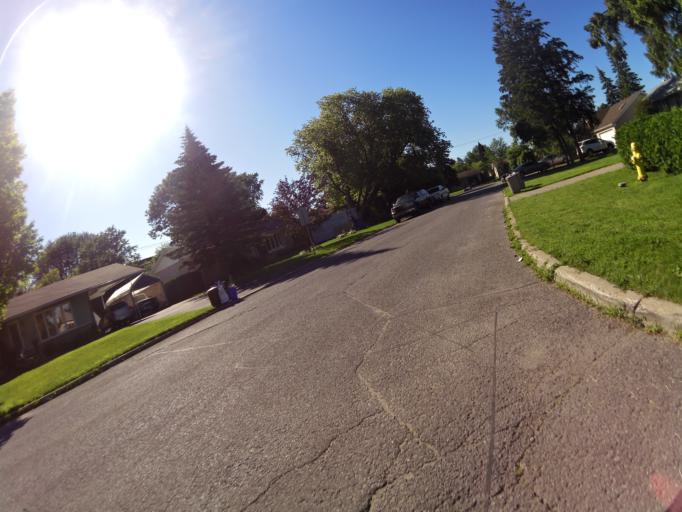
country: CA
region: Ontario
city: Bells Corners
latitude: 45.3317
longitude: -75.7534
